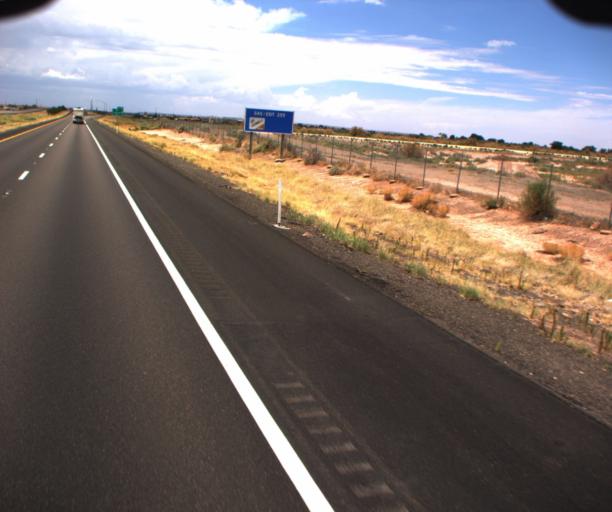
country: US
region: Arizona
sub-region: Navajo County
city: Winslow
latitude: 35.0155
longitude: -110.6653
